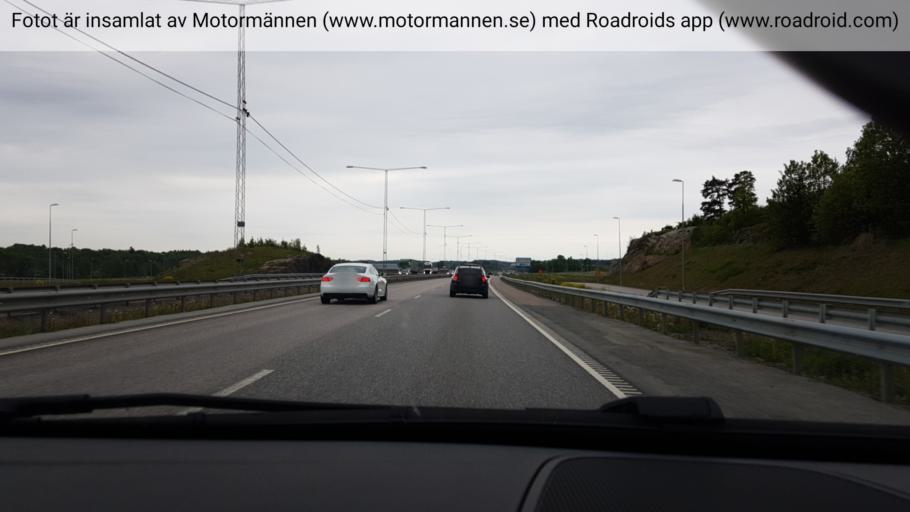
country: SE
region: Stockholm
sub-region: Sigtuna Kommun
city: Rosersberg
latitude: 59.5781
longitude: 17.8998
